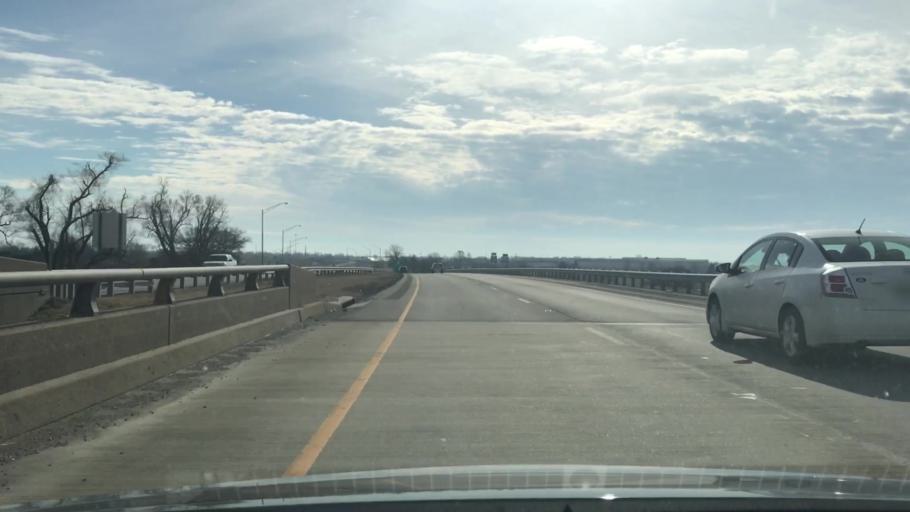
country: US
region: Kentucky
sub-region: Daviess County
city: Owensboro
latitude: 37.7496
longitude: -87.1561
